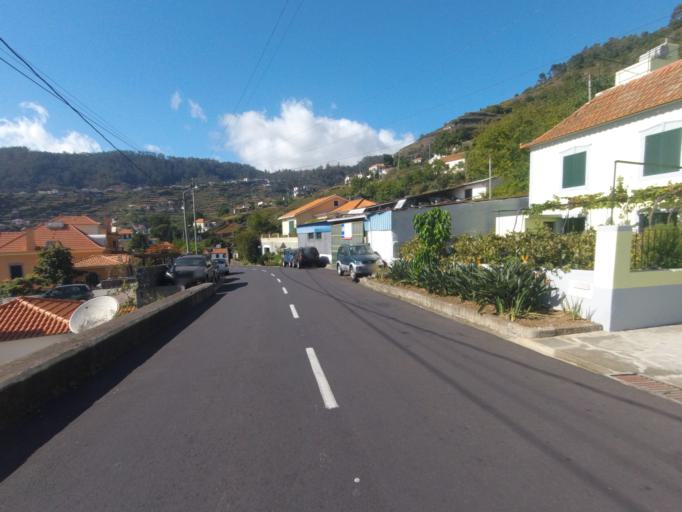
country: PT
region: Madeira
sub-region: Ribeira Brava
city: Campanario
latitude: 32.6717
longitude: -17.0215
